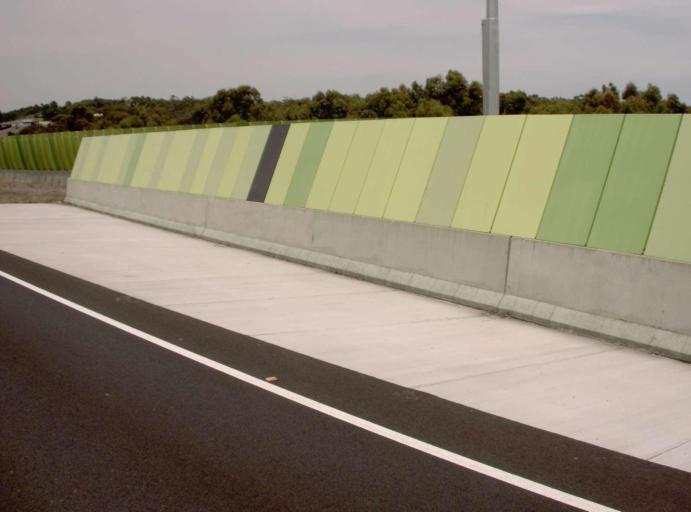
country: AU
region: Victoria
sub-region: Frankston
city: Carrum Downs
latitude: -38.1214
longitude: 145.1722
